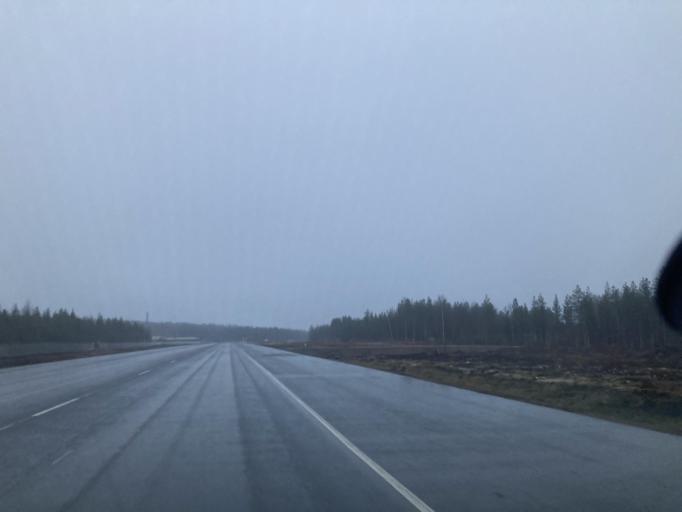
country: FI
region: Lapland
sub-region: Rovaniemi
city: Rovaniemi
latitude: 66.5645
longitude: 25.7960
